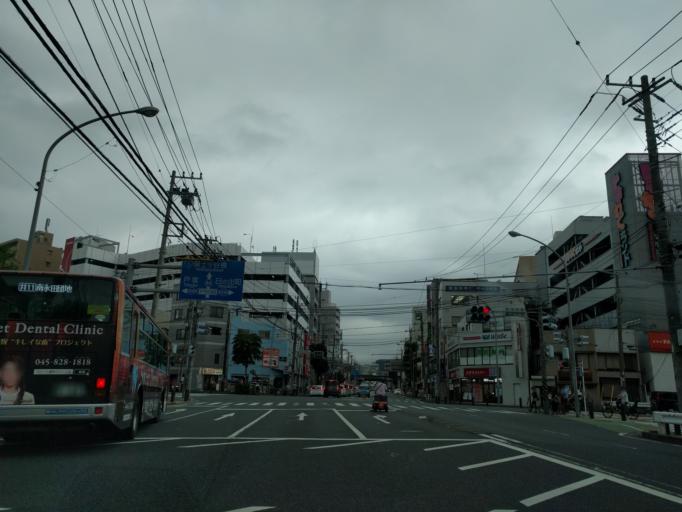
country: JP
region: Kanagawa
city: Yokohama
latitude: 35.4320
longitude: 139.6028
